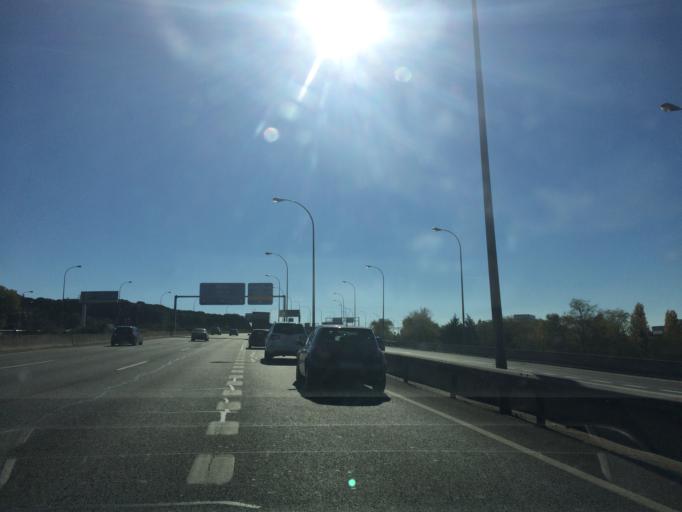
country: ES
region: Madrid
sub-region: Provincia de Madrid
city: Las Tablas
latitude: 40.5186
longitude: -3.6529
